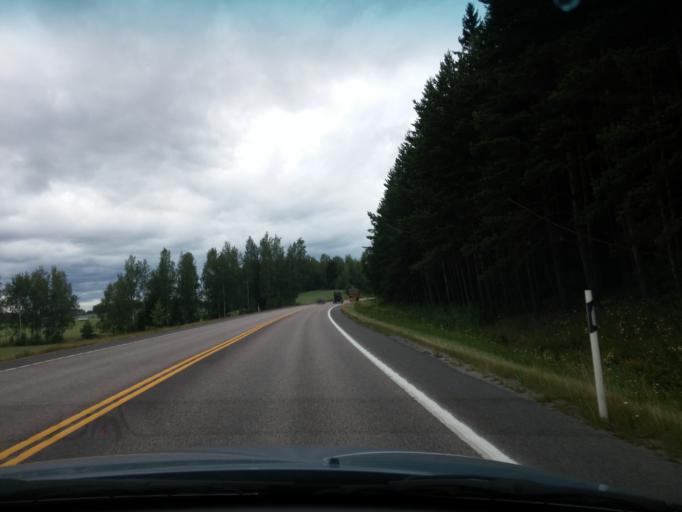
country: FI
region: Uusimaa
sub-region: Porvoo
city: Askola
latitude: 60.4693
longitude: 25.5705
